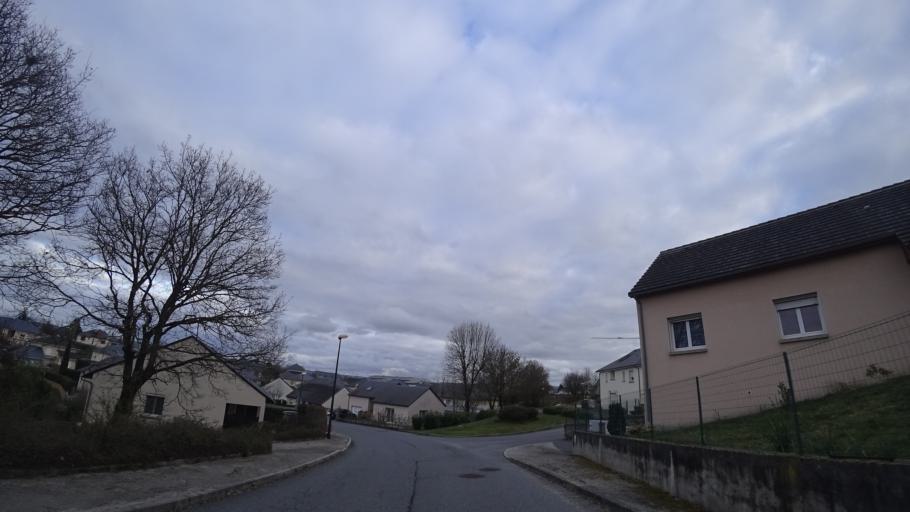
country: FR
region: Midi-Pyrenees
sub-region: Departement de l'Aveyron
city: Le Monastere
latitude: 44.3363
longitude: 2.5733
